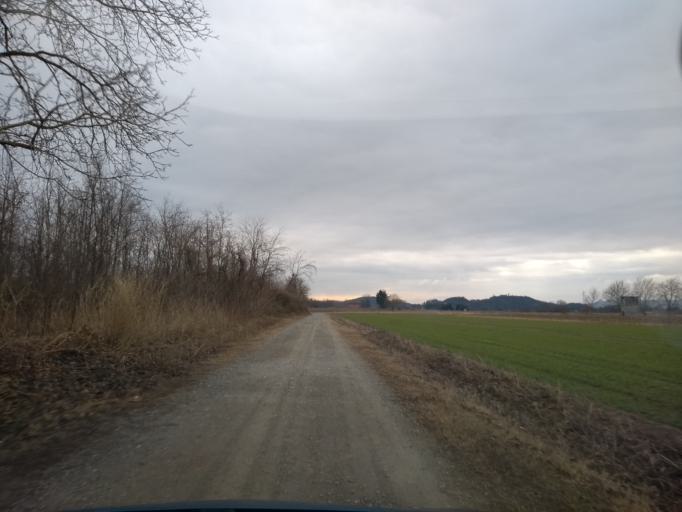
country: IT
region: Piedmont
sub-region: Provincia di Torino
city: Fiorano Canavese
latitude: 45.4863
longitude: 7.8403
